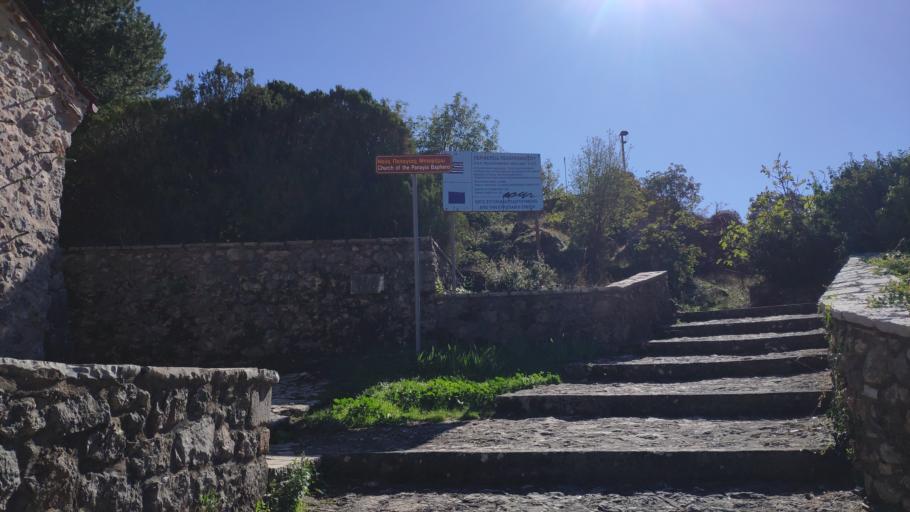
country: GR
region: Peloponnese
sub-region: Nomos Arkadias
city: Dimitsana
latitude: 37.5527
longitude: 22.0796
